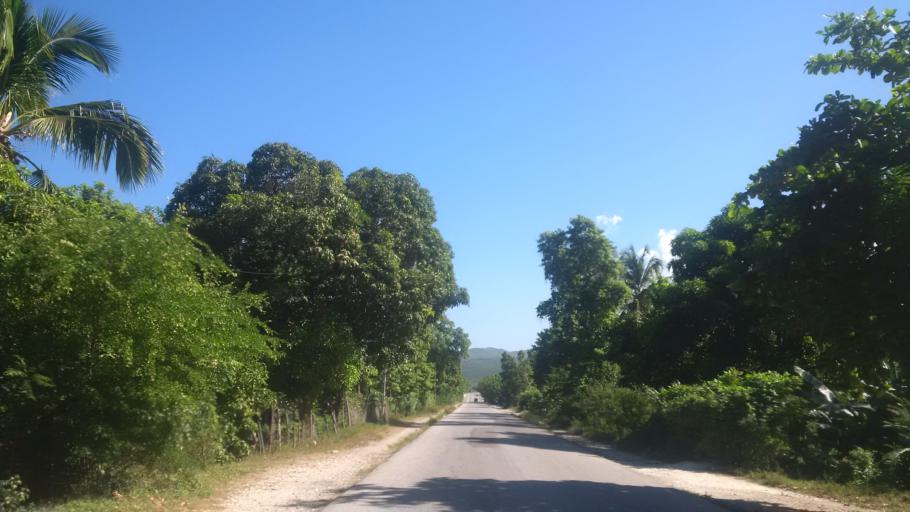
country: HT
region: Ouest
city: Grangwav
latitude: 18.4243
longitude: -72.7214
